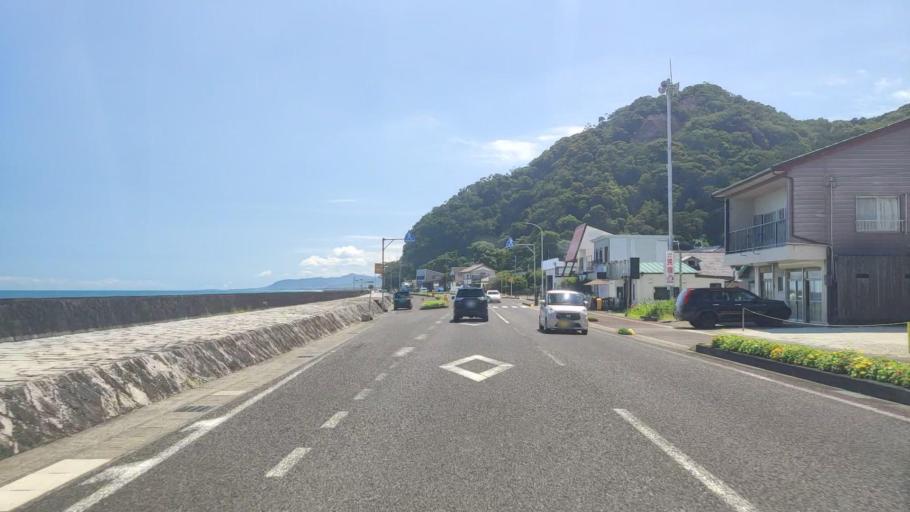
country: JP
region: Wakayama
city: Shingu
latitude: 33.8820
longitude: 136.0958
